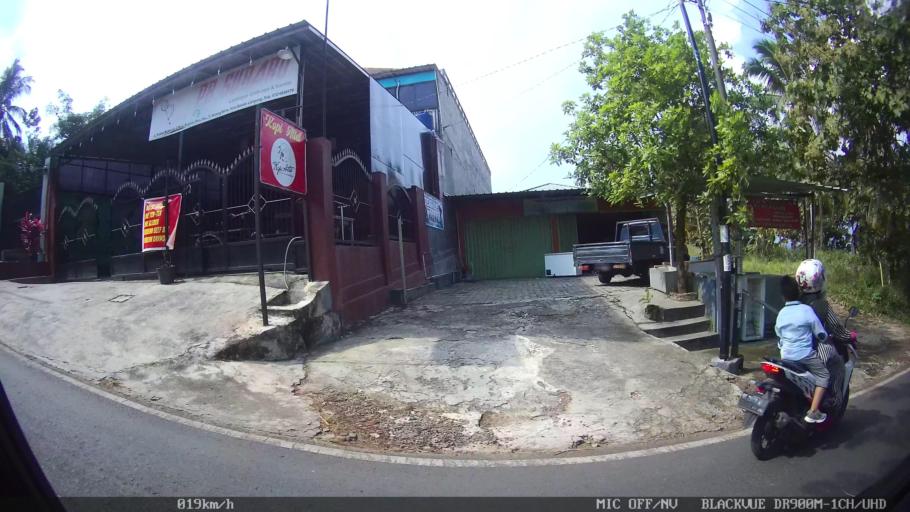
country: ID
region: Lampung
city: Bandarlampung
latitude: -5.4078
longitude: 105.2236
